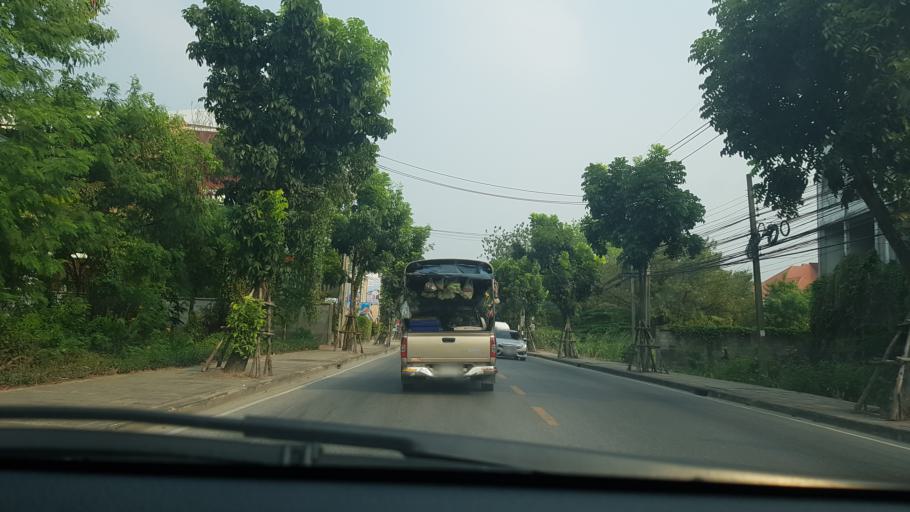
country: TH
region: Bangkok
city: Phasi Charoen
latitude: 13.7565
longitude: 100.3936
